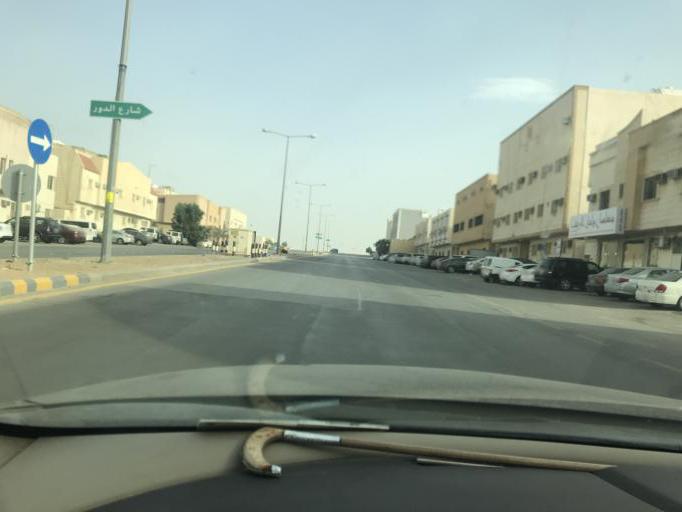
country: SA
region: Ar Riyad
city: Riyadh
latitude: 24.7829
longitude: 46.7149
